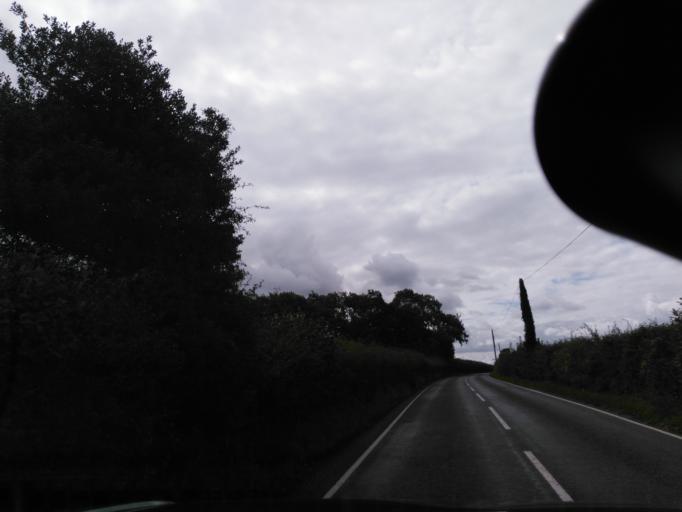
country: GB
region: England
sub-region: Dorset
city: Blandford Forum
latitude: 50.8966
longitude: -2.1559
